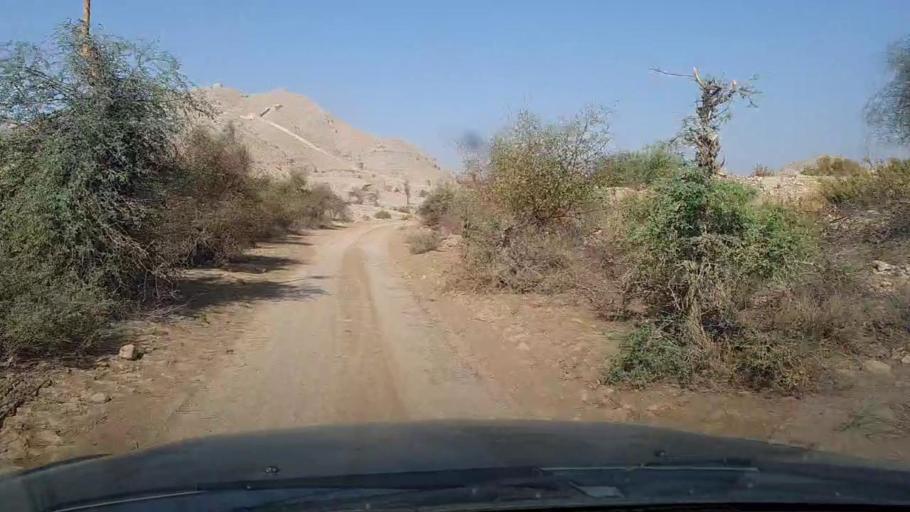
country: PK
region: Sindh
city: Sann
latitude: 25.8832
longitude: 67.9373
